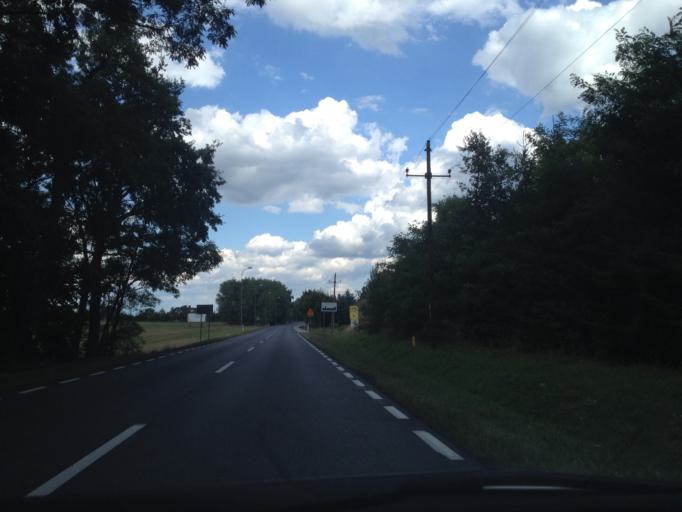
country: PL
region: Lubusz
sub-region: Powiat zarski
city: Sieniawa Zarska
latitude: 51.5930
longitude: 15.0872
